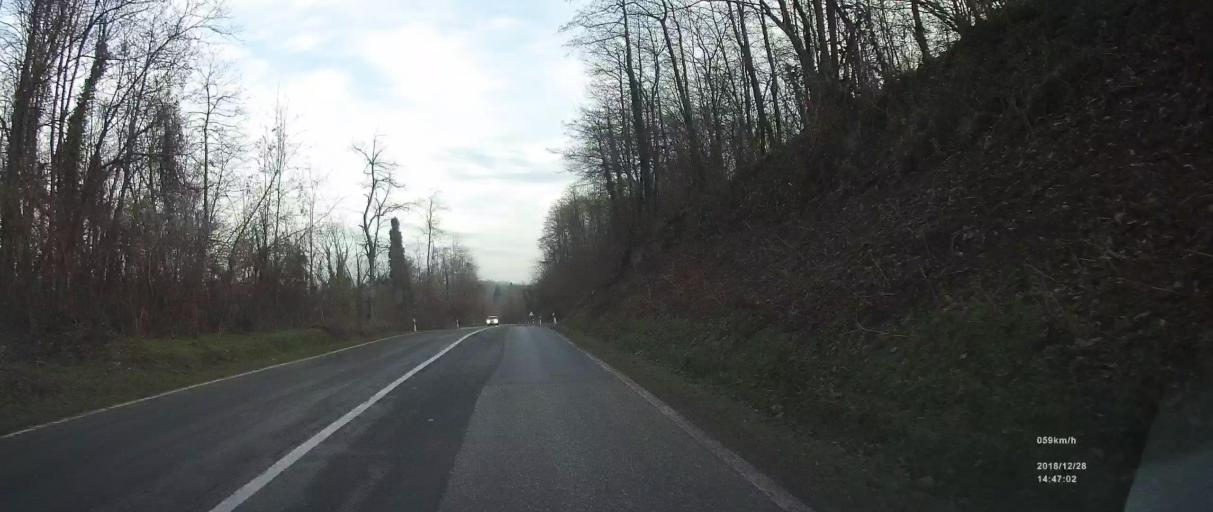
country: SI
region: Crnomelj
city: Crnomelj
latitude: 45.4470
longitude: 15.3232
